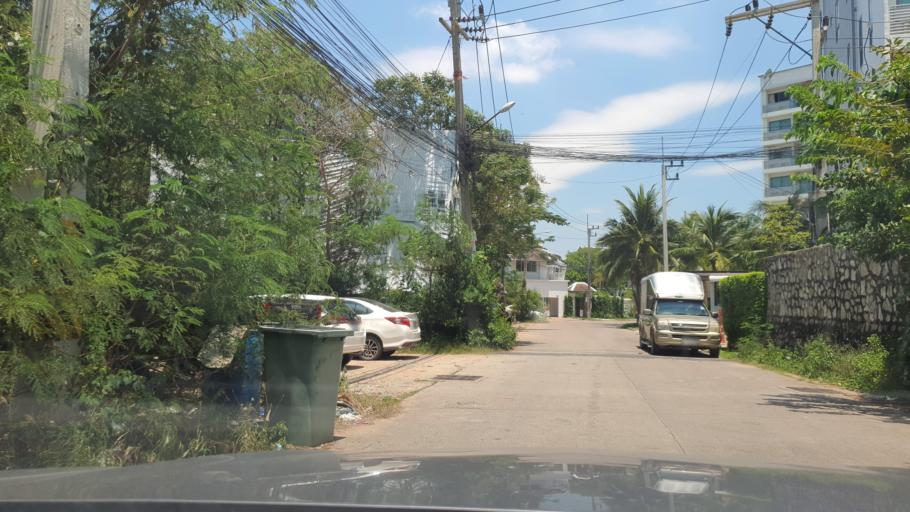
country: TH
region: Chon Buri
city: Phatthaya
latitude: 12.8952
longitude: 100.8786
